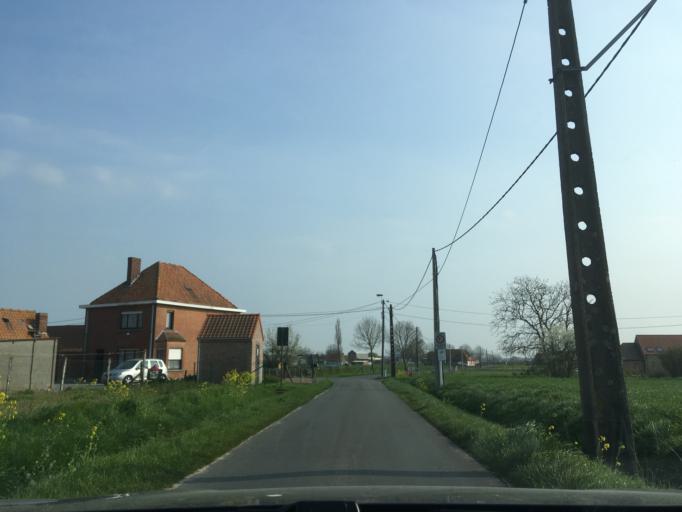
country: BE
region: Flanders
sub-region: Provincie West-Vlaanderen
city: Izegem
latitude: 50.9480
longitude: 3.2174
